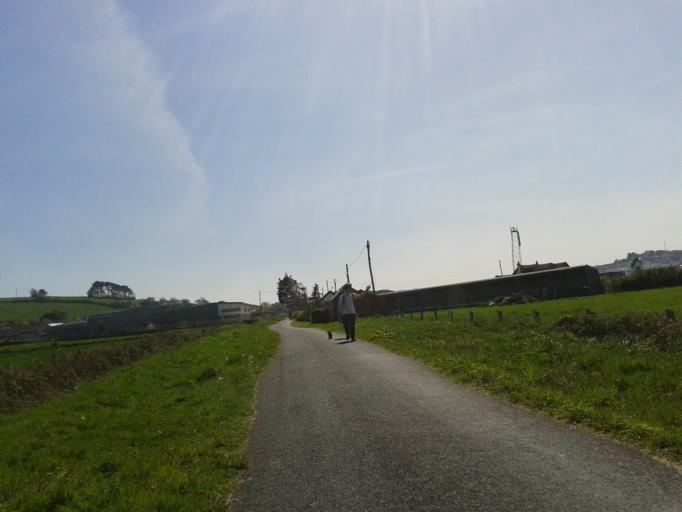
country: GB
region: England
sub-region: Devon
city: Appledore
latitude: 51.0619
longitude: -4.1760
